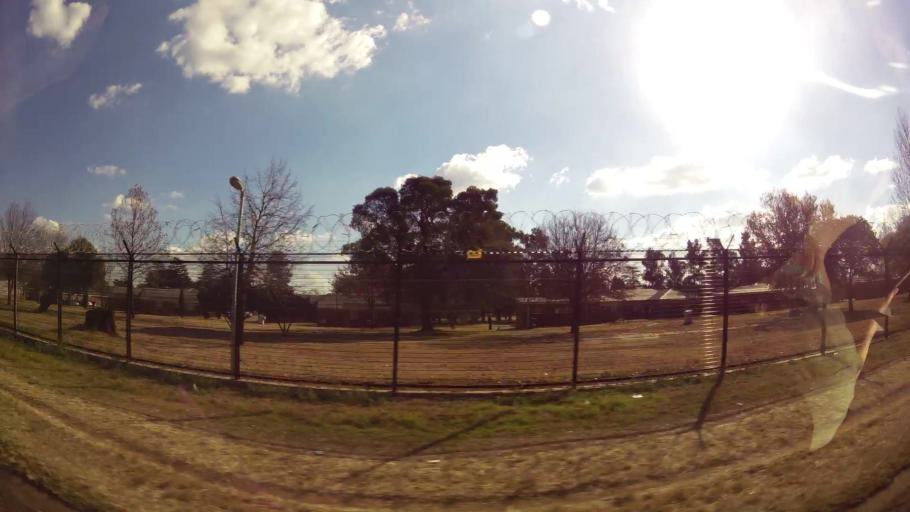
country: ZA
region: Mpumalanga
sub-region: Nkangala District Municipality
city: Witbank
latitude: -25.8887
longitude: 29.2213
